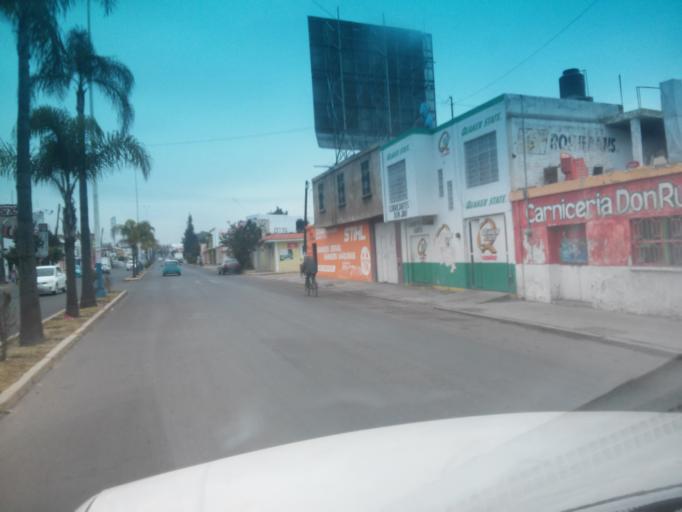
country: MX
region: Durango
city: Victoria de Durango
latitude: 24.0097
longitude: -104.6789
